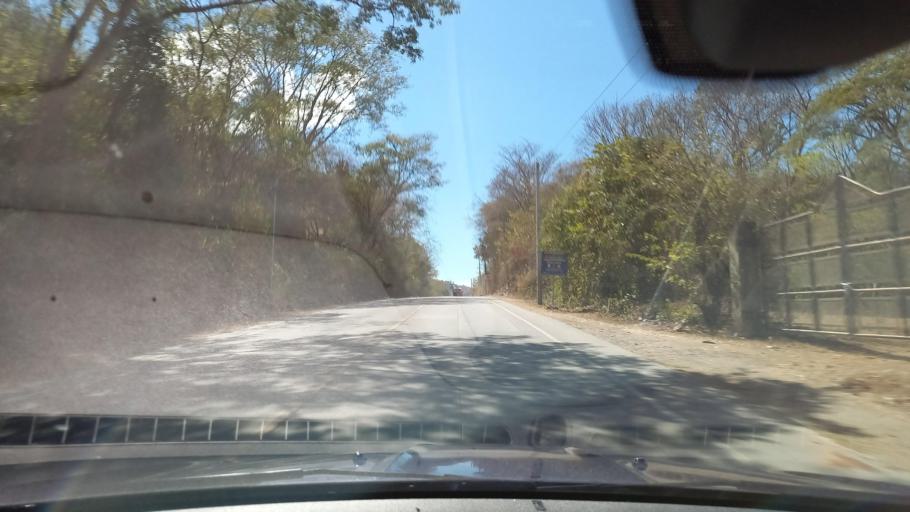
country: SV
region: Santa Ana
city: Metapan
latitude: 14.3471
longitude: -89.4534
